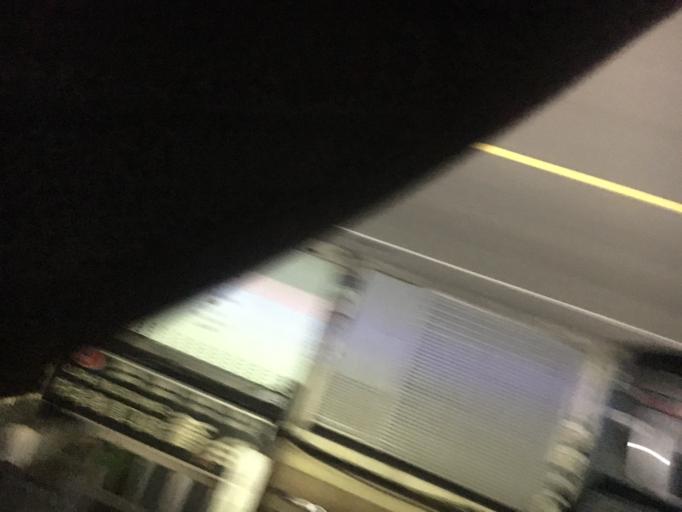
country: TW
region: Taiwan
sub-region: Hsinchu
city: Hsinchu
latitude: 24.7936
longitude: 120.9700
